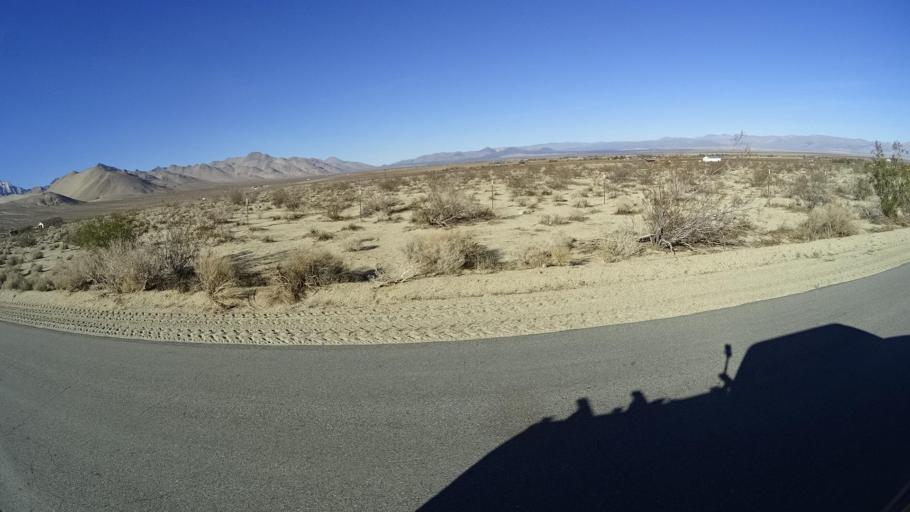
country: US
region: California
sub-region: Kern County
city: Inyokern
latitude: 35.6811
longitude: -117.8562
